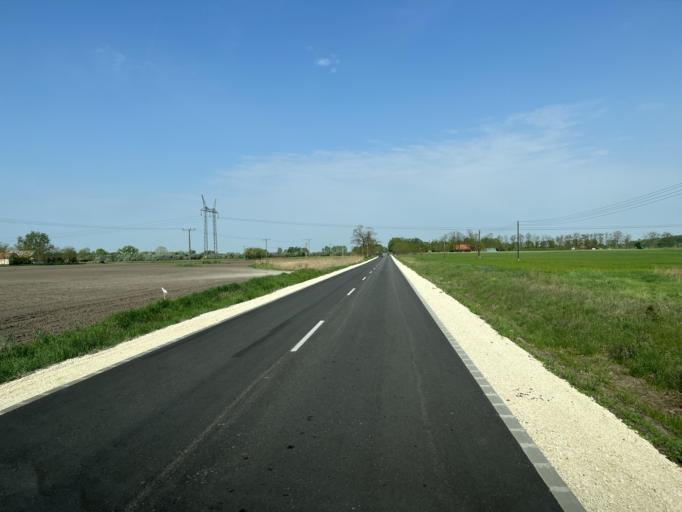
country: HU
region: Pest
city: Kocser
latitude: 46.9938
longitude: 19.9522
